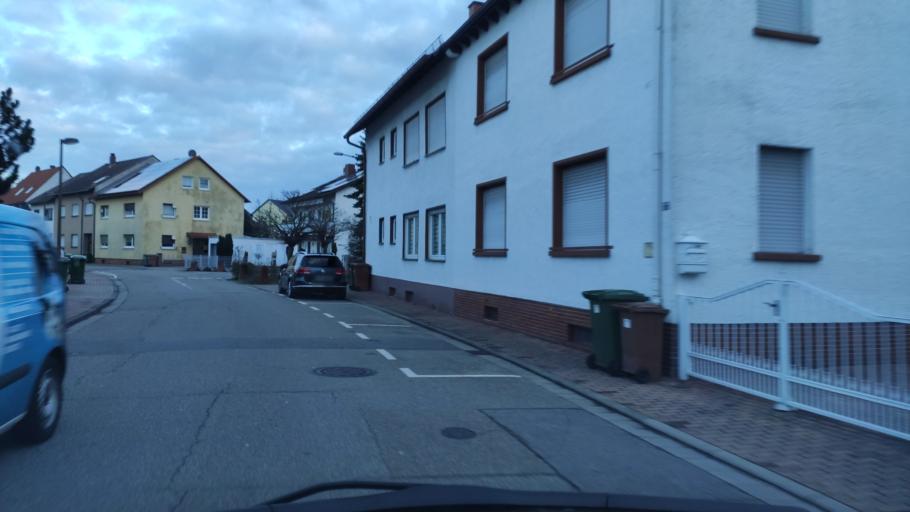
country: DE
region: Baden-Wuerttemberg
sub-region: Karlsruhe Region
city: Hockenheim
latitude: 49.3181
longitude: 8.5581
